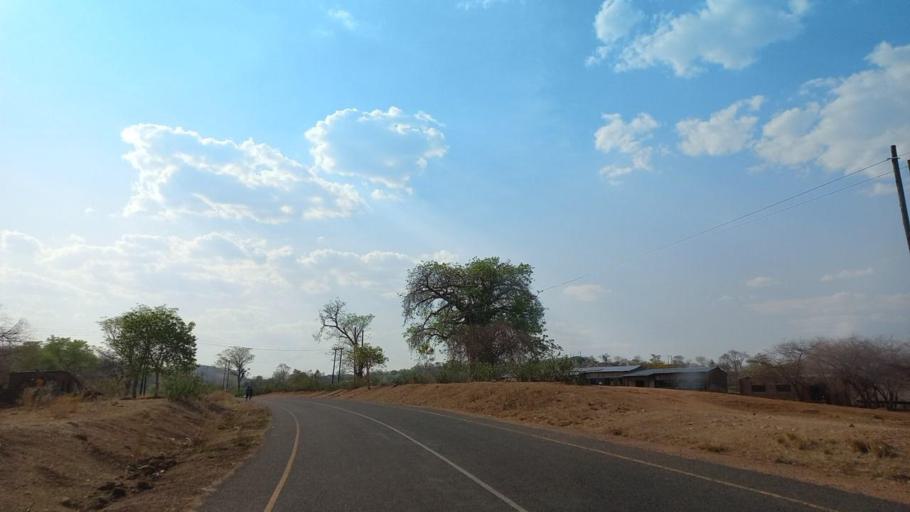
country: ZM
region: Lusaka
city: Luangwa
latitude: -14.9887
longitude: 30.2115
